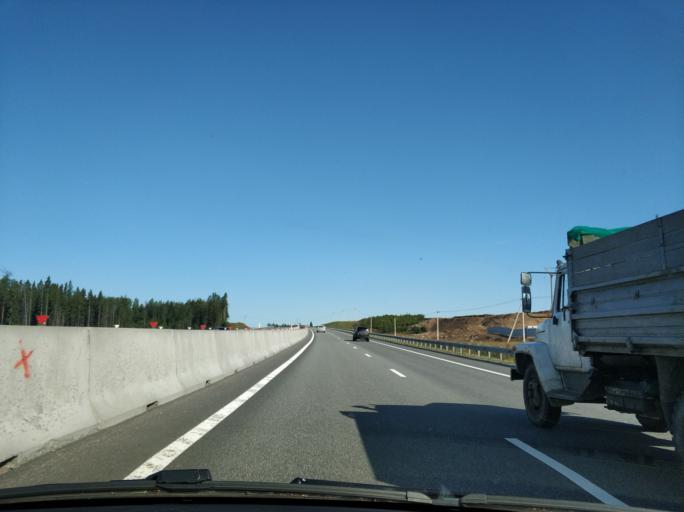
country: RU
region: Leningrad
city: Sosnovo
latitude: 60.5101
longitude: 30.1895
